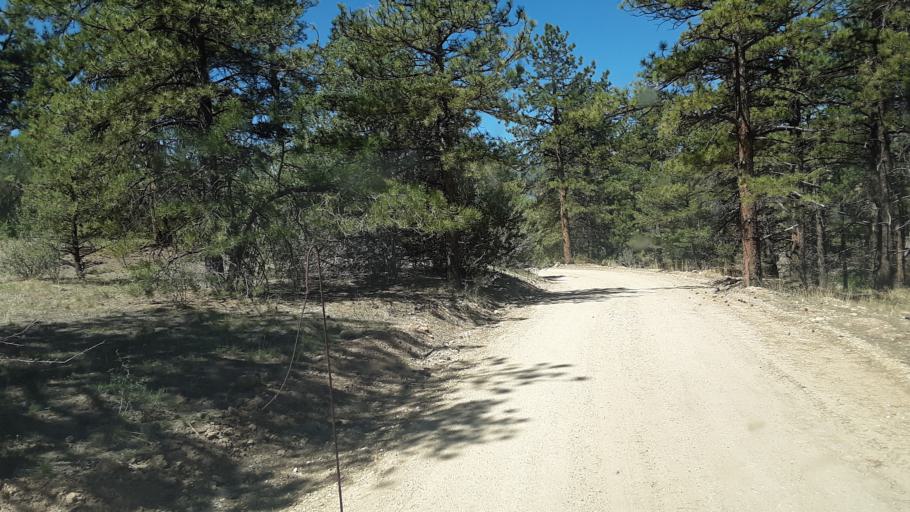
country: US
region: Colorado
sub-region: Custer County
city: Westcliffe
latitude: 38.2529
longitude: -105.5628
